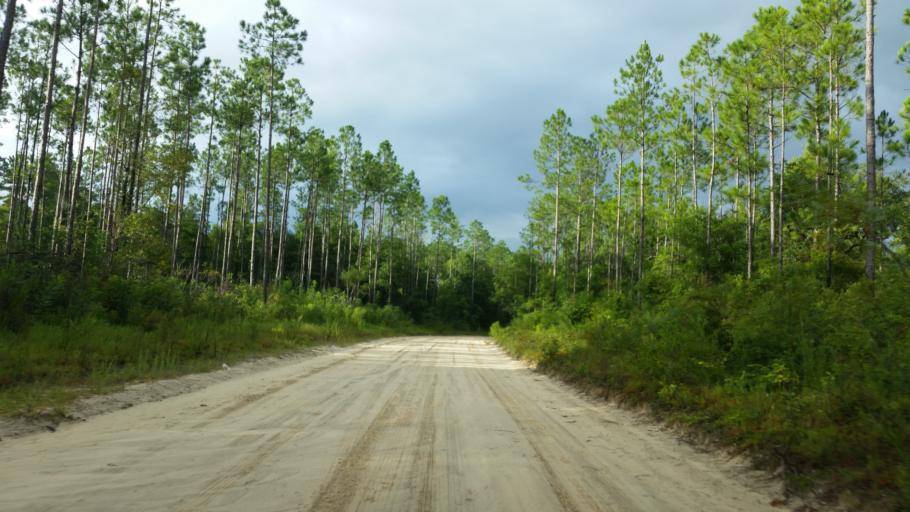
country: US
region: Florida
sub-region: Okaloosa County
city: Crestview
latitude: 30.6628
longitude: -86.7644
